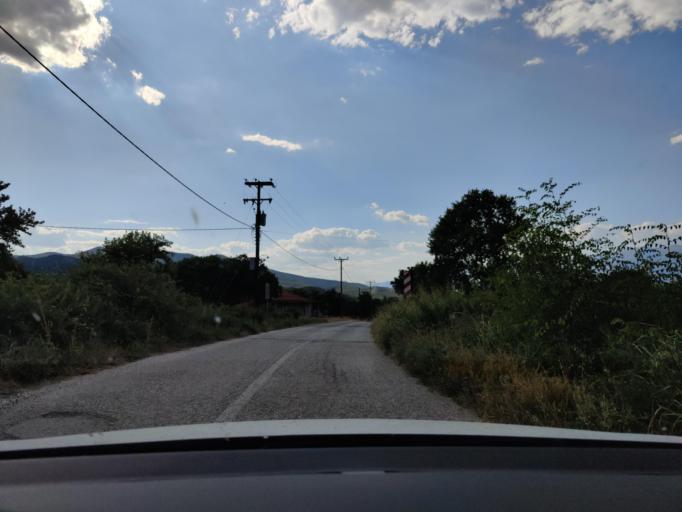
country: GR
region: Central Macedonia
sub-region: Nomos Serron
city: Chrysochorafa
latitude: 41.1767
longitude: 23.1152
